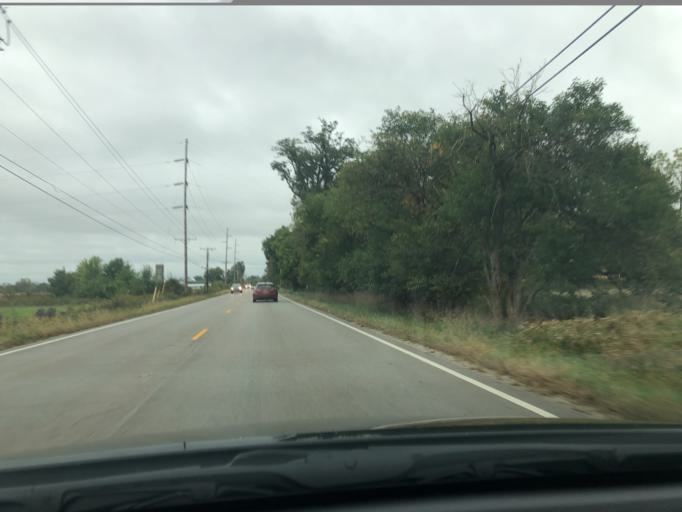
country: US
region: Ohio
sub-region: Union County
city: Marysville
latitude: 40.2432
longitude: -83.3304
